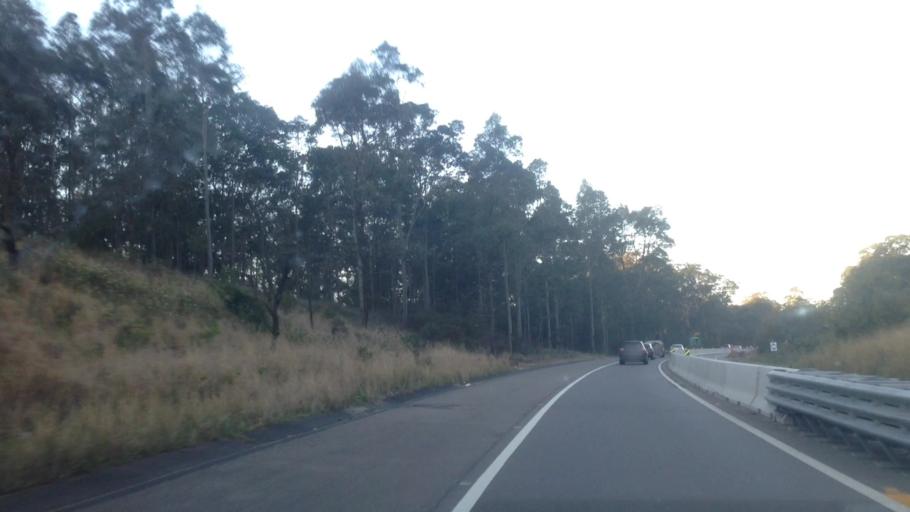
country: AU
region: New South Wales
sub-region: Wyong Shire
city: Jilliby
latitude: -33.2167
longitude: 151.4420
